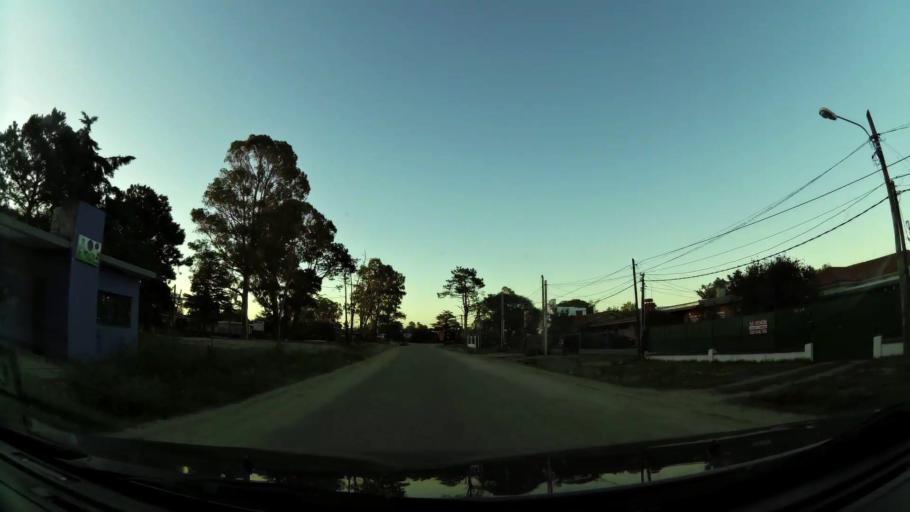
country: UY
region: Canelones
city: Barra de Carrasco
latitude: -34.8427
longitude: -55.9775
